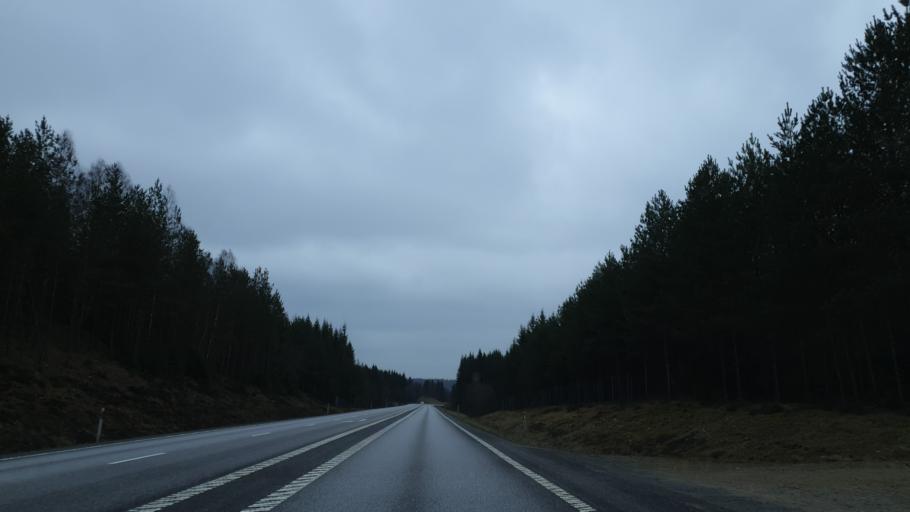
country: SE
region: Vaestra Goetaland
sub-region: Boras Kommun
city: Viskafors
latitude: 57.6085
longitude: 12.8722
